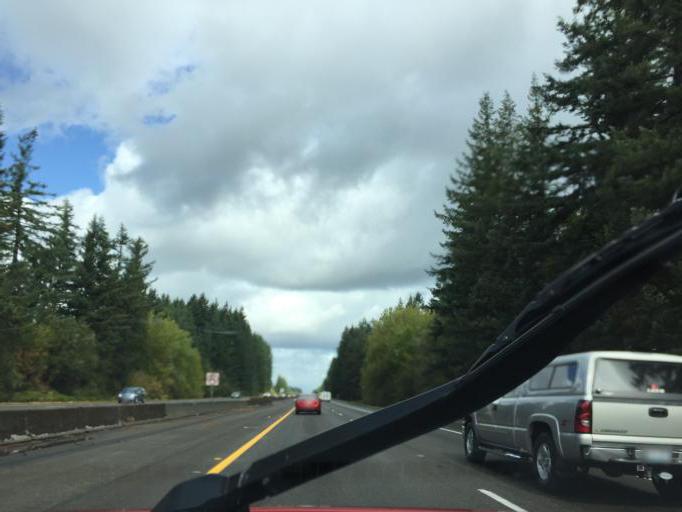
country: US
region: Washington
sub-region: Lewis County
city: Winlock
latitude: 46.5102
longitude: -122.8766
